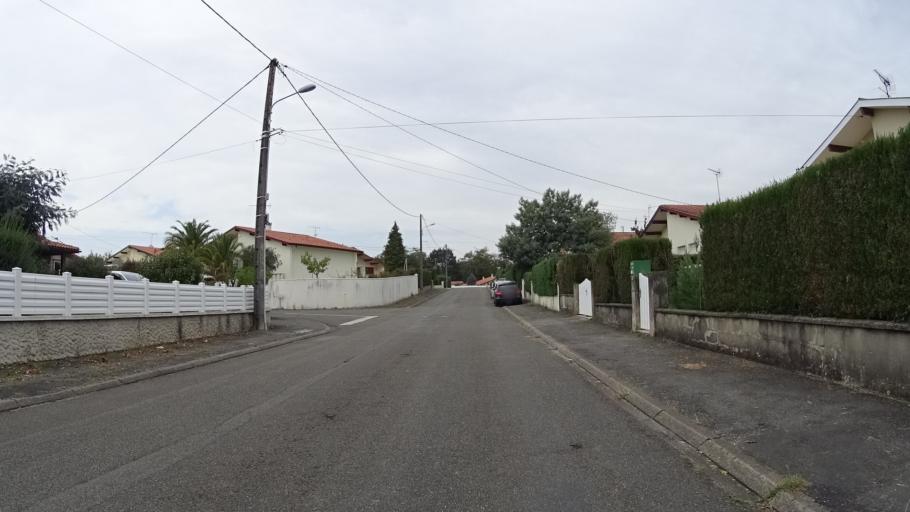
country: FR
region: Aquitaine
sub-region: Departement des Landes
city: Saint-Paul-les-Dax
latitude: 43.7287
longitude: -1.0727
